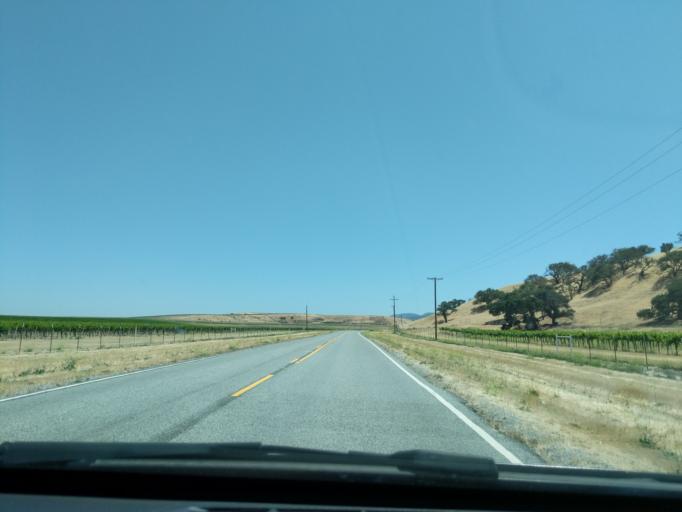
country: US
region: California
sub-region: Monterey County
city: King City
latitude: 36.1736
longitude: -121.1318
